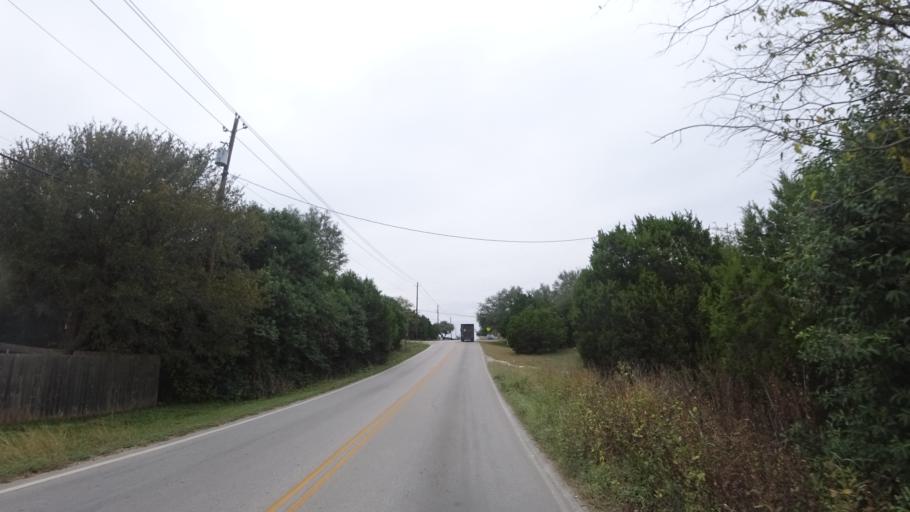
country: US
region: Texas
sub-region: Travis County
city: Lakeway
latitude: 30.3724
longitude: -97.9369
